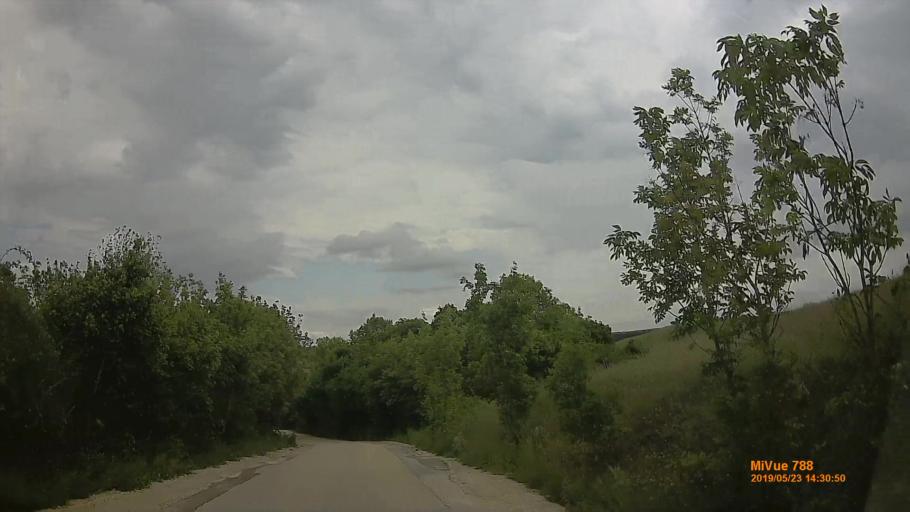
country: HU
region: Veszprem
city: Nemesvamos
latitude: 47.1051
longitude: 17.8596
